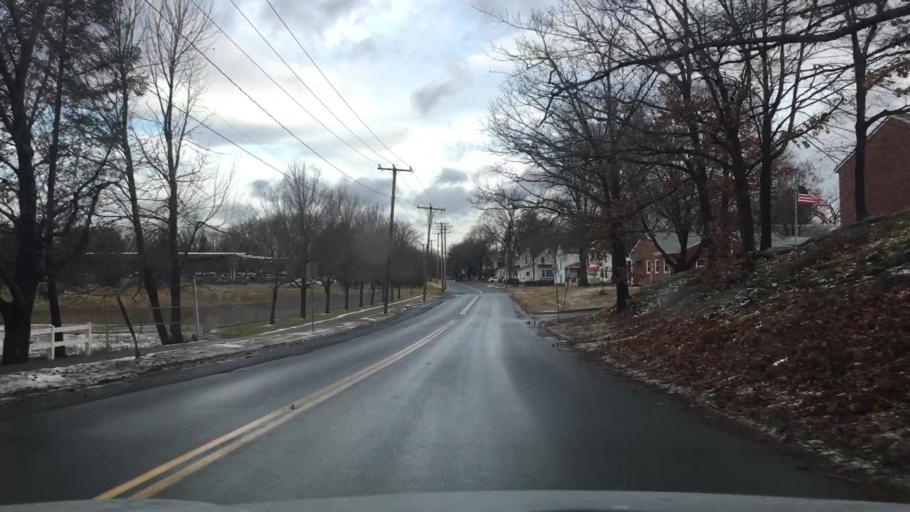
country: US
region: Massachusetts
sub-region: Franklin County
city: Greenfield
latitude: 42.5953
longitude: -72.6113
